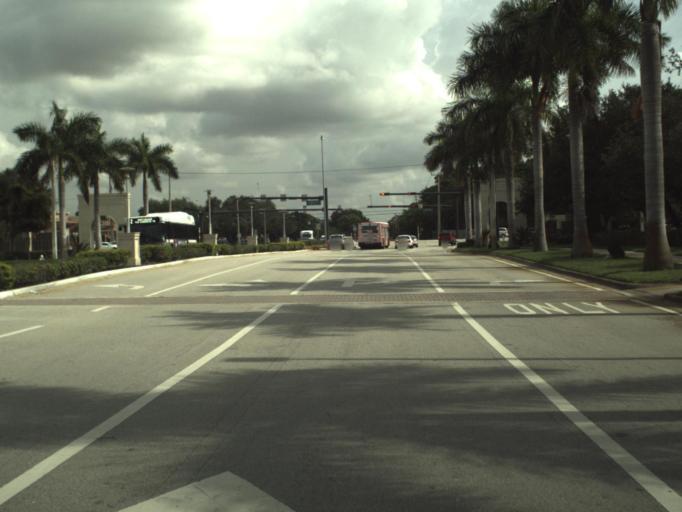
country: US
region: Florida
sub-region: Palm Beach County
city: Highland Beach
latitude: 26.3926
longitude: -80.1023
